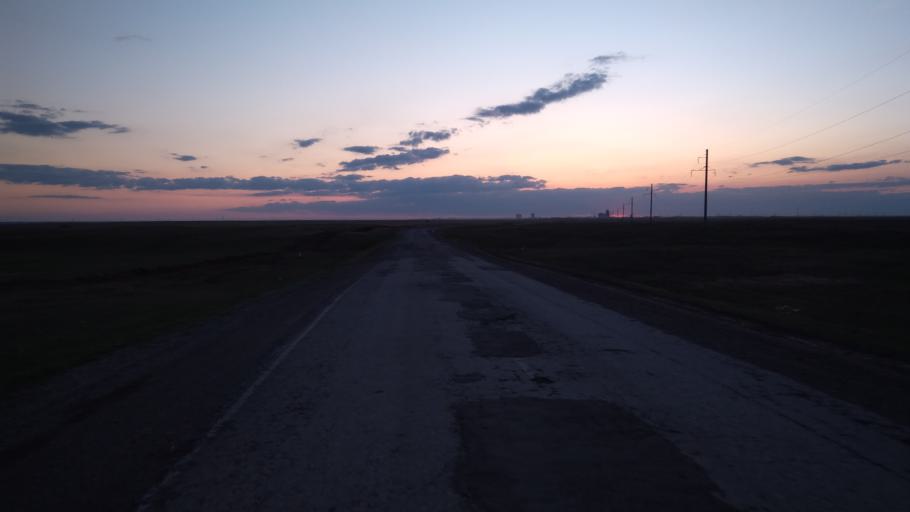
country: RU
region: Chelyabinsk
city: Troitsk
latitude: 54.0867
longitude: 61.6616
